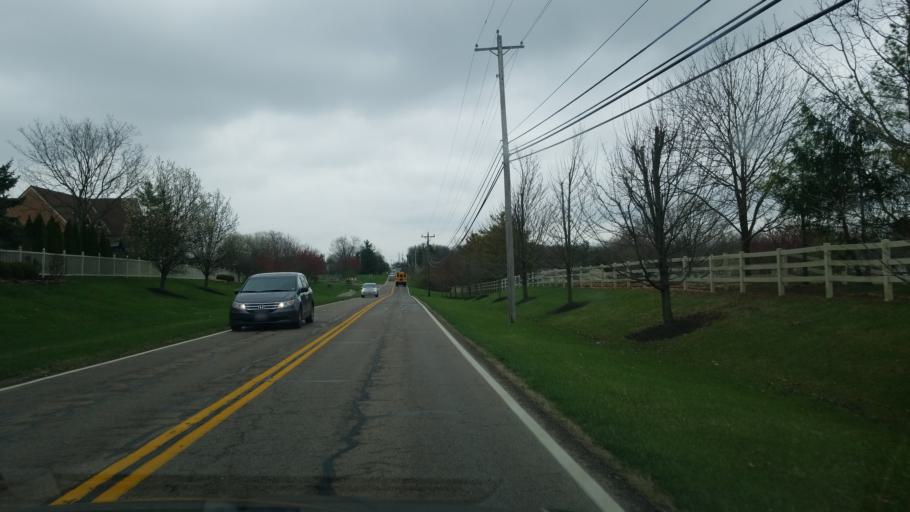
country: US
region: Ohio
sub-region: Butler County
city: Beckett Ridge
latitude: 39.3726
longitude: -84.4329
